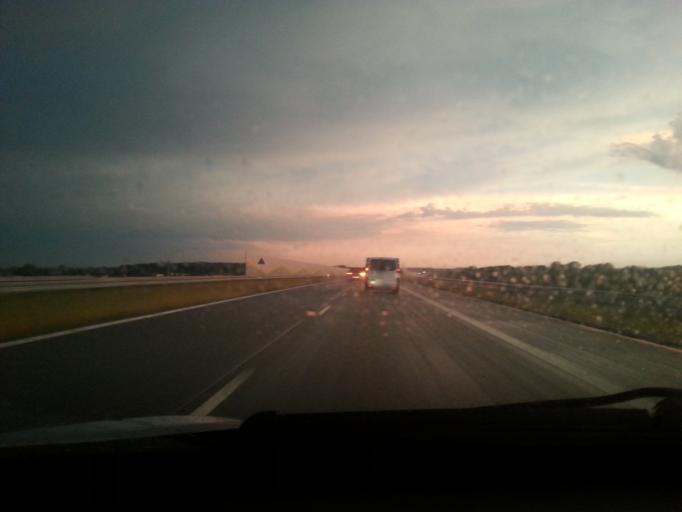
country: PL
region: Lodz Voivodeship
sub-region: Powiat laski
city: Lask
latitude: 51.5674
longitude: 19.1614
